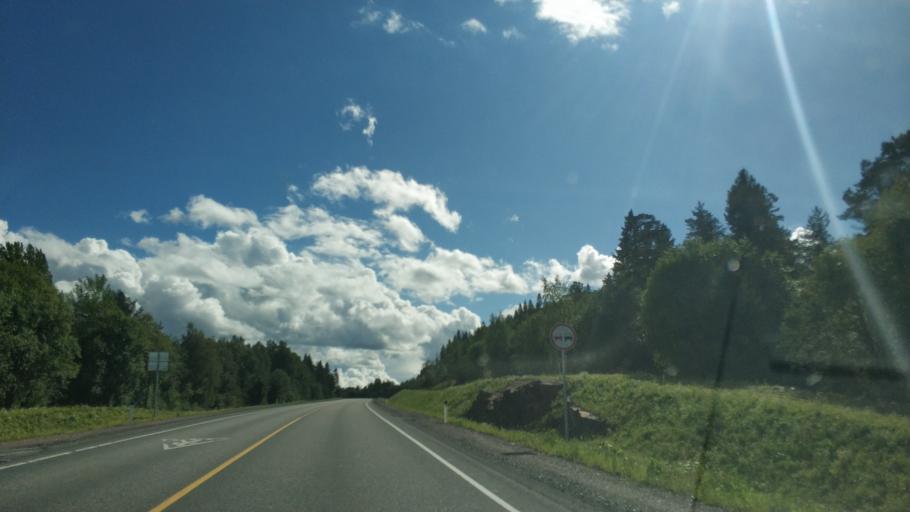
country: RU
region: Republic of Karelia
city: Ruskeala
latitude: 61.9014
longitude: 30.6350
